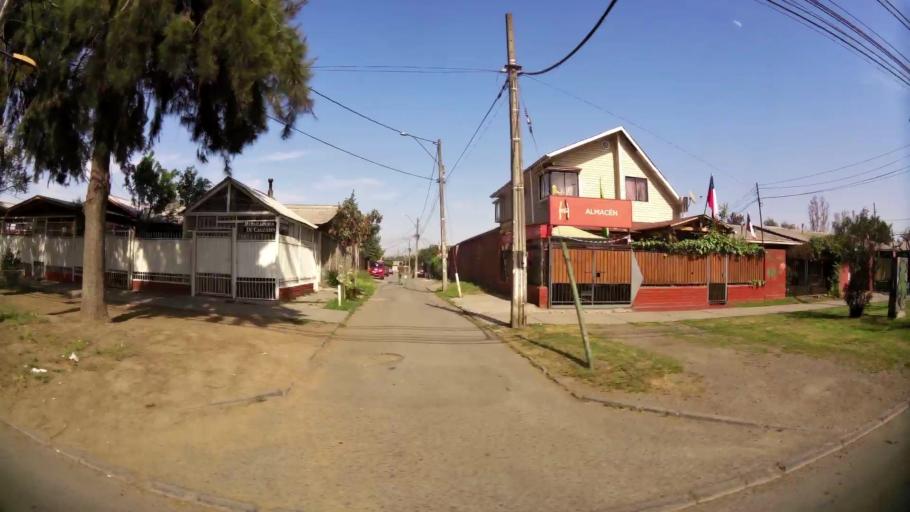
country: CL
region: Santiago Metropolitan
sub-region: Provincia de Santiago
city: Lo Prado
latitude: -33.4799
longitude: -70.7403
